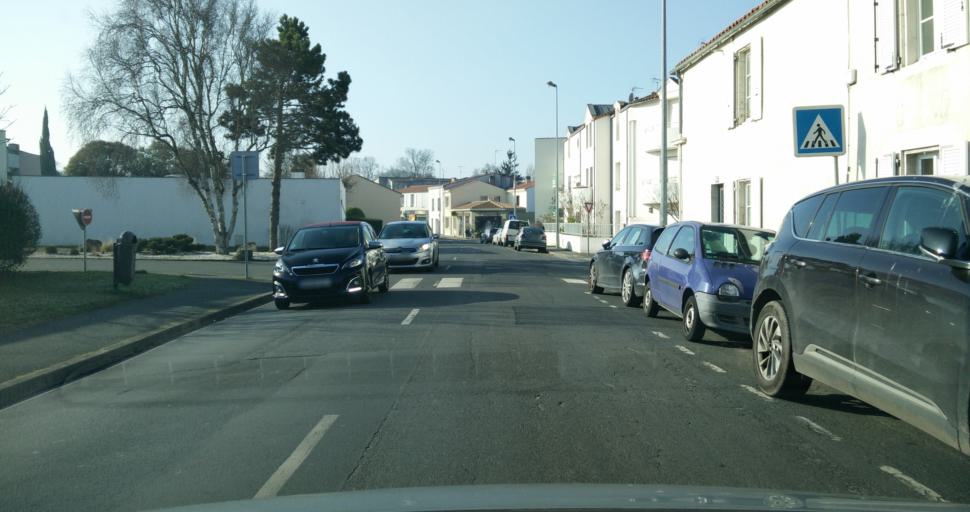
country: FR
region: Poitou-Charentes
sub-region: Departement de la Charente-Maritime
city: La Rochelle
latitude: 46.1730
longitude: -1.1466
